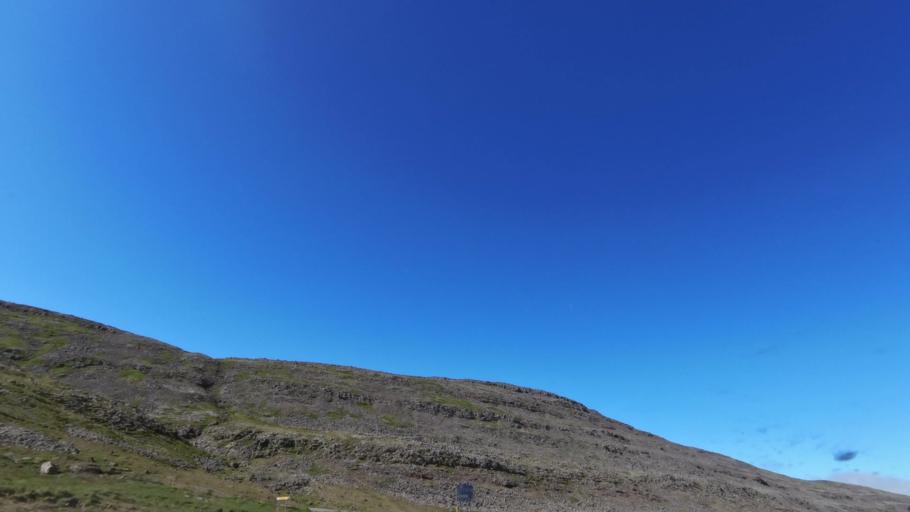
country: IS
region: West
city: Olafsvik
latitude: 65.5622
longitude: -24.1782
